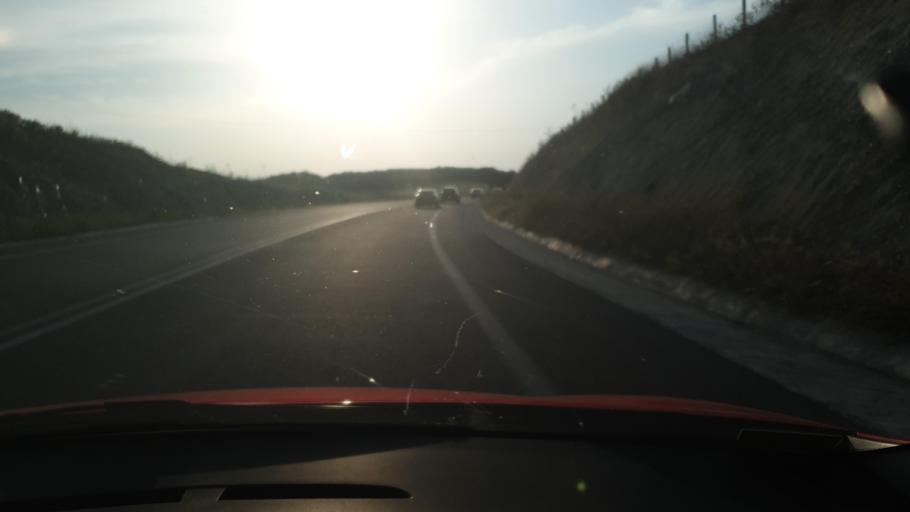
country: GR
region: Central Macedonia
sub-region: Nomos Chalkidikis
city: Galatista
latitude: 40.4620
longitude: 23.2261
